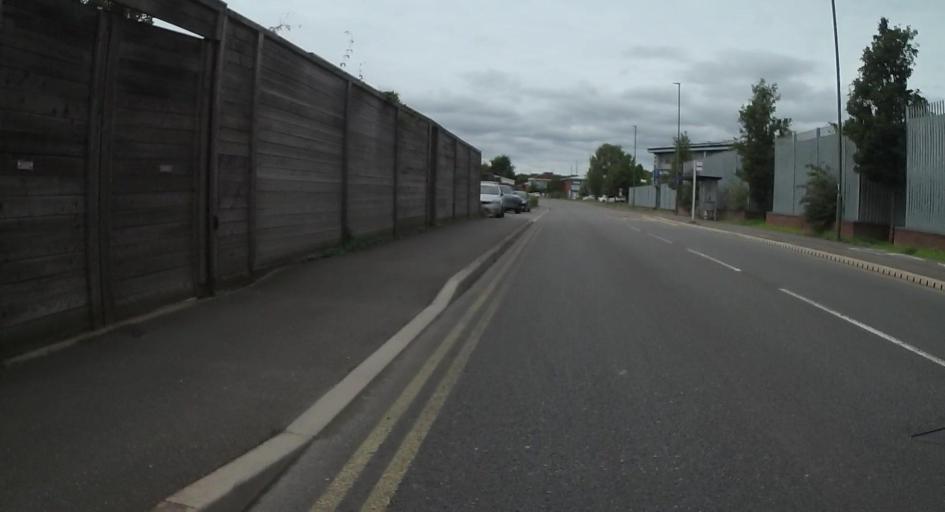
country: GB
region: England
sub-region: Surrey
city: Woking
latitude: 51.3267
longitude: -0.5388
